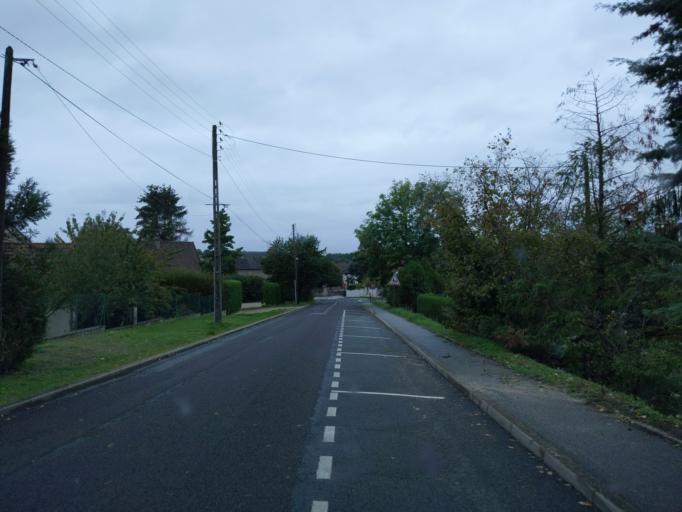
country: FR
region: Ile-de-France
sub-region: Departement des Yvelines
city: Saint-Arnoult-en-Yvelines
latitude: 48.5747
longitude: 1.9427
